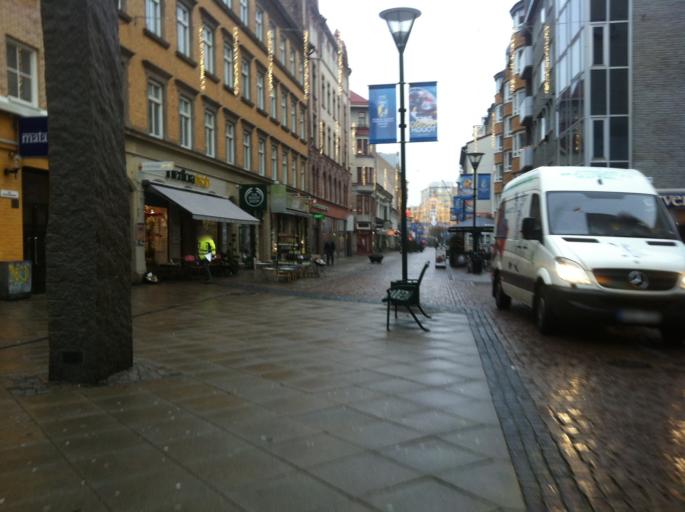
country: SE
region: Skane
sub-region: Malmo
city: Malmoe
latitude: 55.5983
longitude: 13.0011
